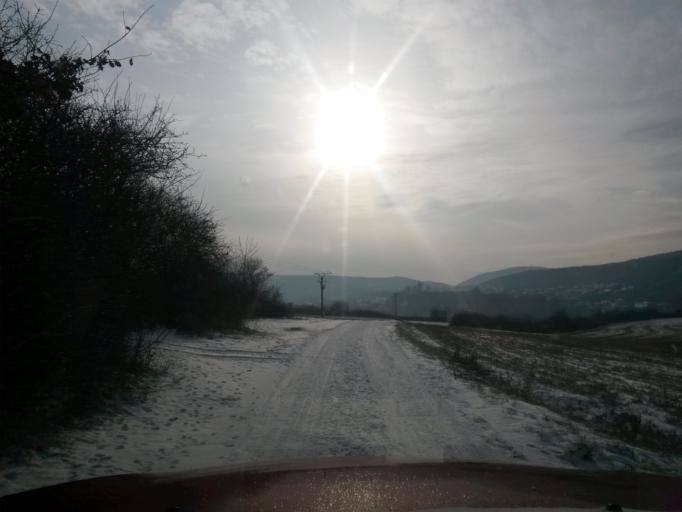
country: SK
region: Kosicky
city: Kosice
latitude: 48.8092
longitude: 21.2380
